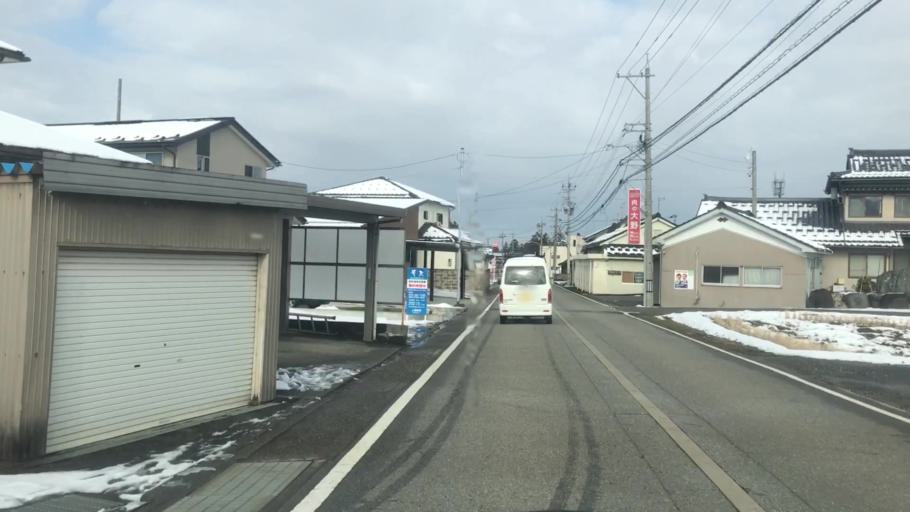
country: JP
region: Toyama
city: Toyama-shi
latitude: 36.6271
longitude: 137.2506
